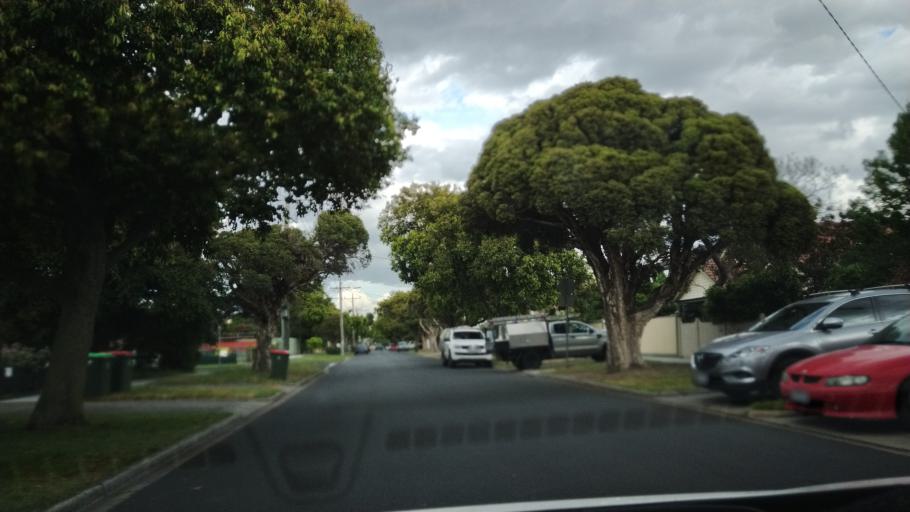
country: AU
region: Victoria
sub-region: Glen Eira
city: Glen Huntly
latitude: -37.9013
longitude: 145.0515
